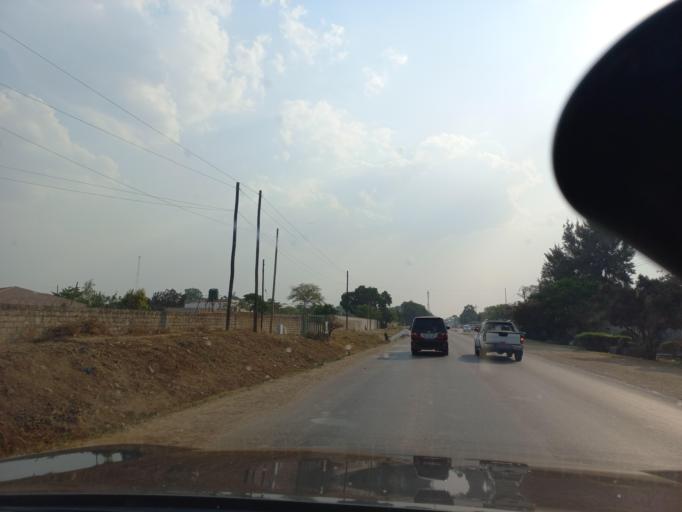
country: ZM
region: Lusaka
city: Lusaka
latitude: -15.4590
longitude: 28.2559
